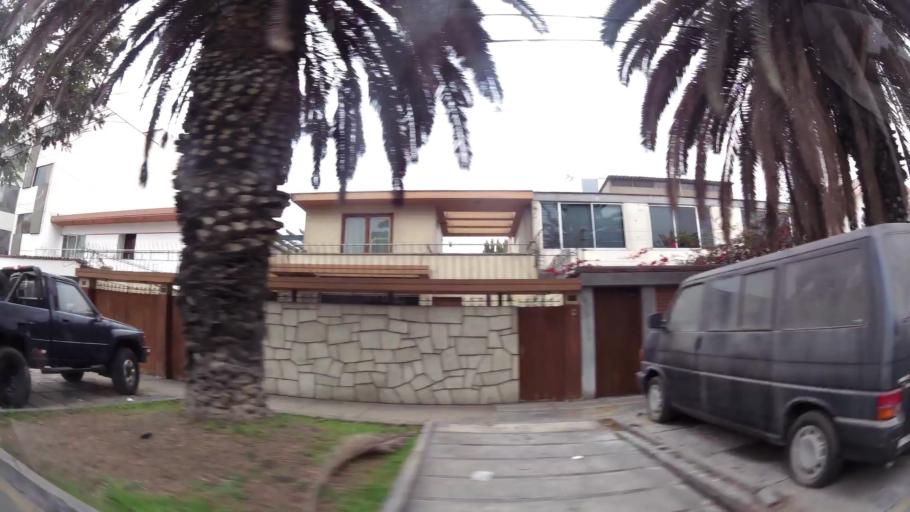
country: PE
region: Lima
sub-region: Lima
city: San Luis
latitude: -12.0905
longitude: -77.0010
